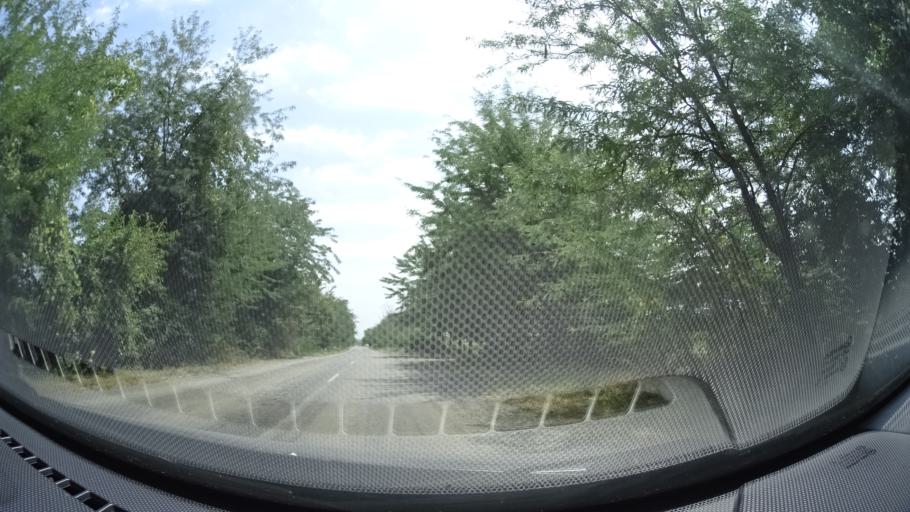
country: GE
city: Bagdadi
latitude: 41.8499
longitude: 46.0472
